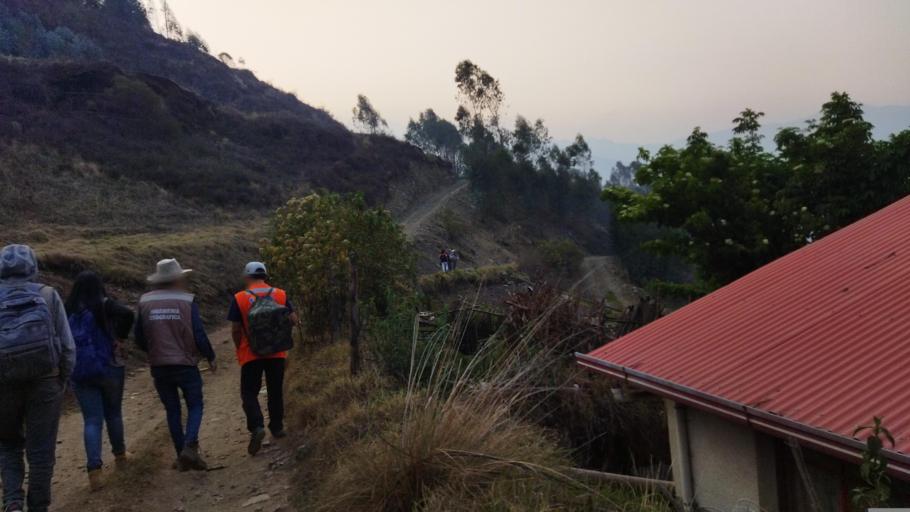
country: BO
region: La Paz
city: Quime
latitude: -16.9841
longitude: -67.1930
